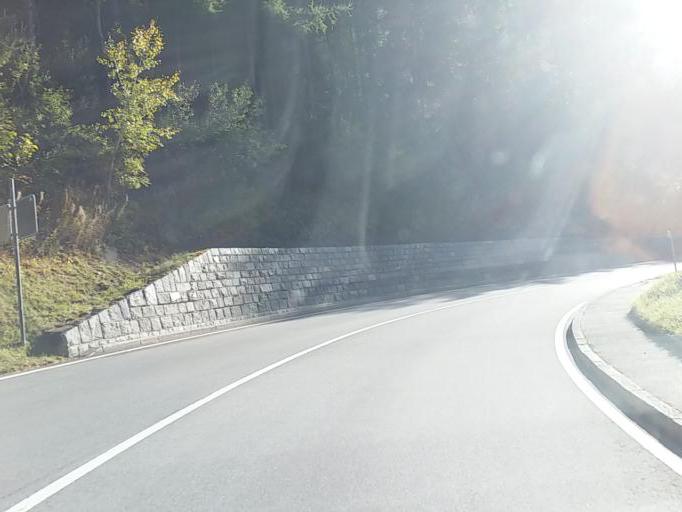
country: CH
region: Valais
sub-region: Brig District
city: Naters
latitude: 46.2945
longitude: 8.0635
